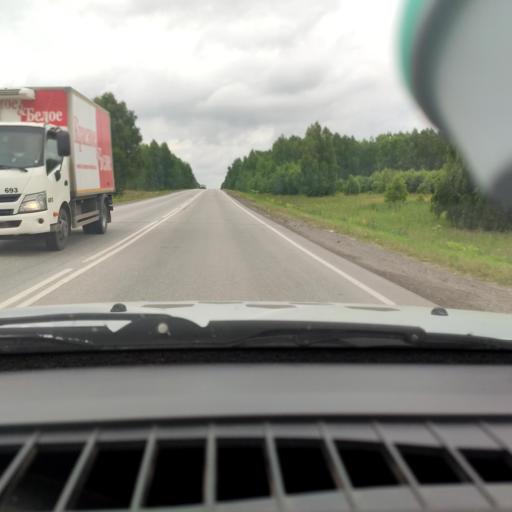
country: RU
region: Perm
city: Kungur
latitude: 57.4526
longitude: 57.0192
